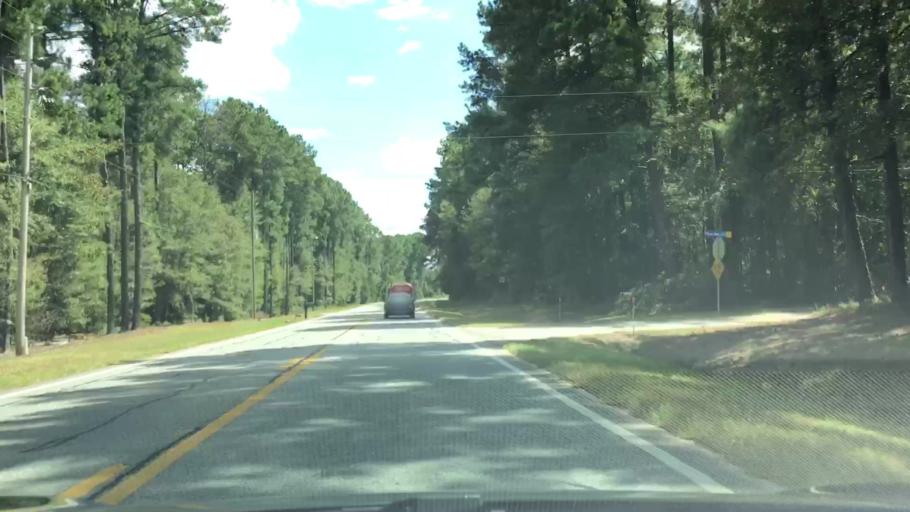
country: US
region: Georgia
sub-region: Oconee County
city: Watkinsville
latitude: 33.7841
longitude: -83.3145
